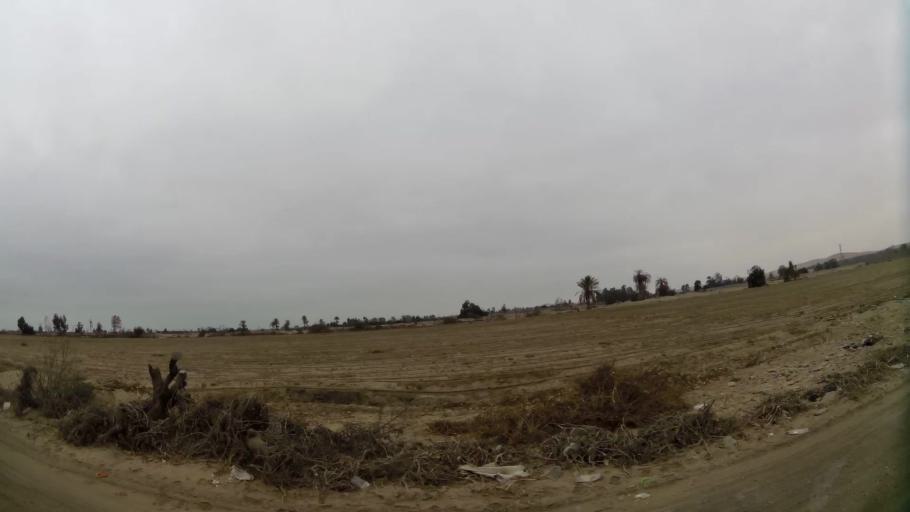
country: PE
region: Ica
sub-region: Provincia de Pisco
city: Villa Tupac Amaru
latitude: -13.7595
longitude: -76.1697
